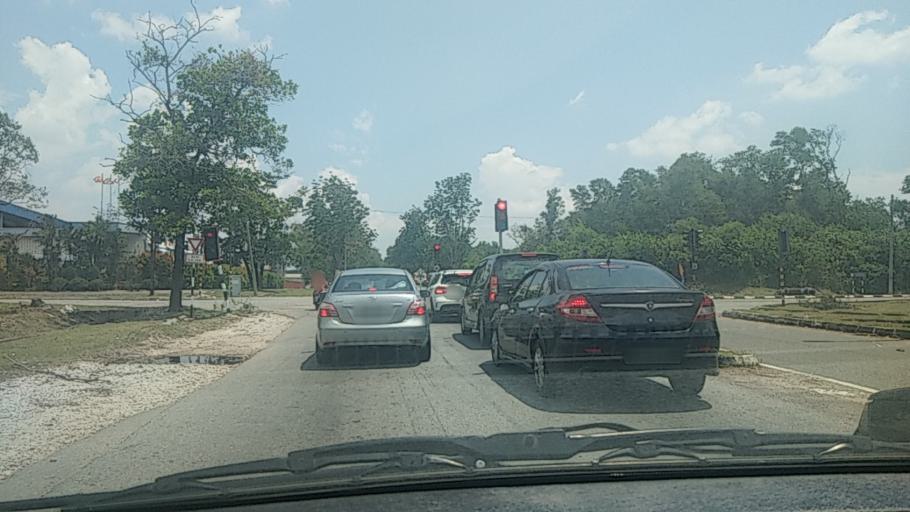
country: MY
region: Kedah
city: Sungai Petani
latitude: 5.6458
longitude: 100.5317
